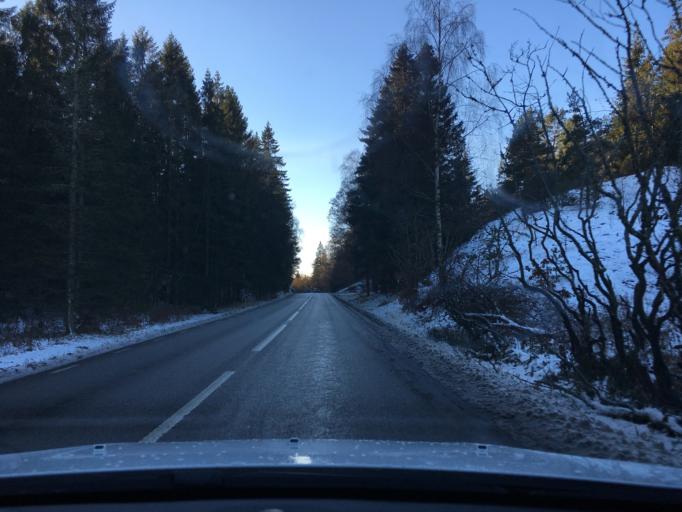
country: SE
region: Vaestra Goetaland
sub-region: Tjorns Kommun
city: Myggenas
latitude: 58.1210
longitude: 11.7154
